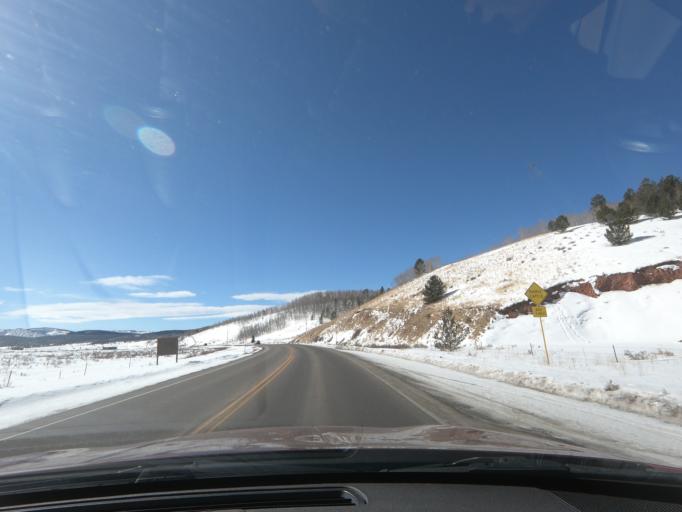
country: US
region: Colorado
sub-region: Teller County
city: Cripple Creek
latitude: 38.7984
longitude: -105.1217
